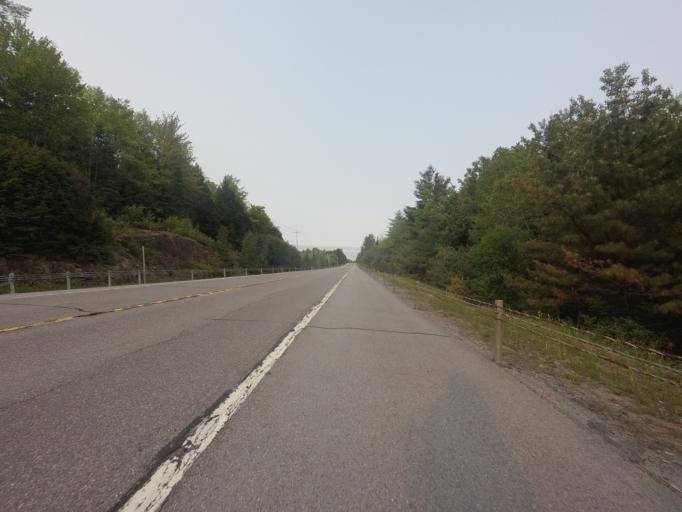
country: US
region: New York
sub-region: Jefferson County
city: Carthage
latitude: 44.0778
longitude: -75.4445
